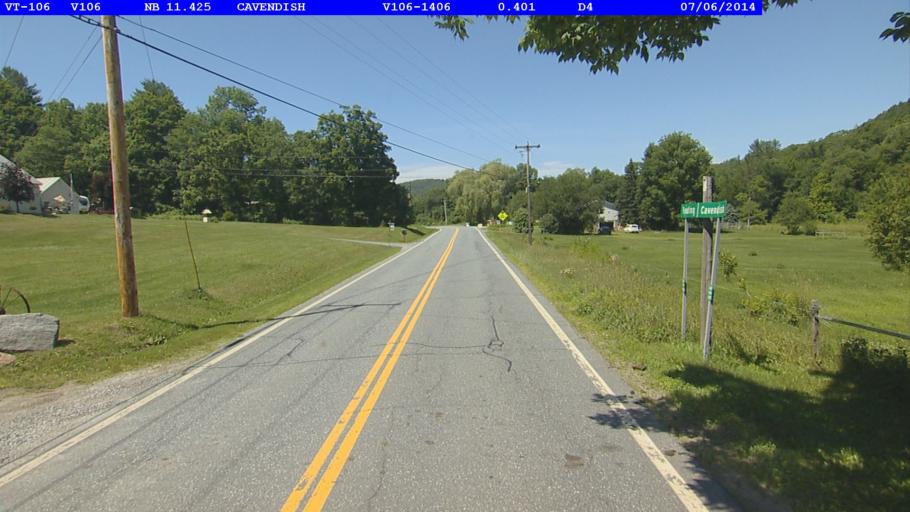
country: US
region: Vermont
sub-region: Windsor County
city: Windsor
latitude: 43.4441
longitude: -72.5345
